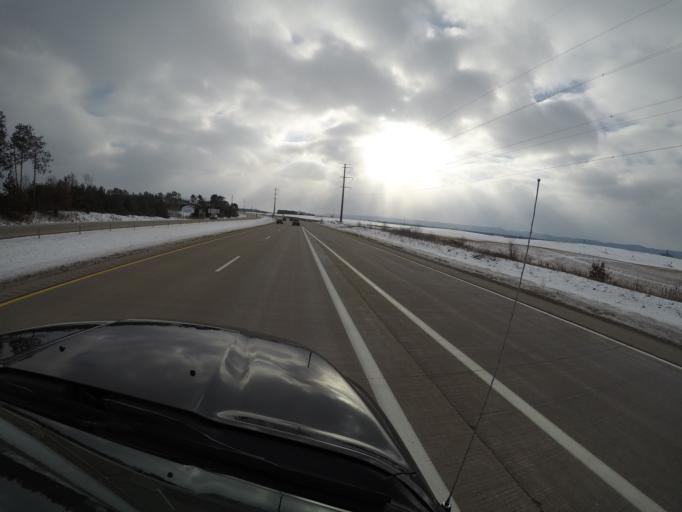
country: US
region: Wisconsin
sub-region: La Crosse County
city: Brice Prairie
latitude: 43.9653
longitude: -91.2863
